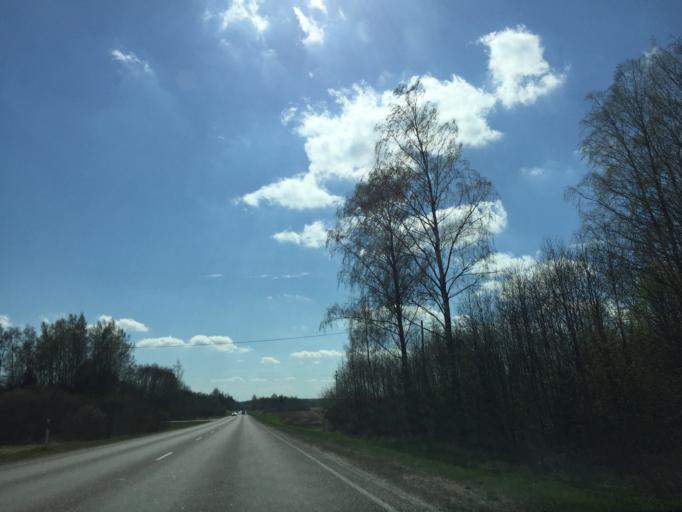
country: EE
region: Tartu
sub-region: Elva linn
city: Elva
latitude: 58.1015
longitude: 26.2328
